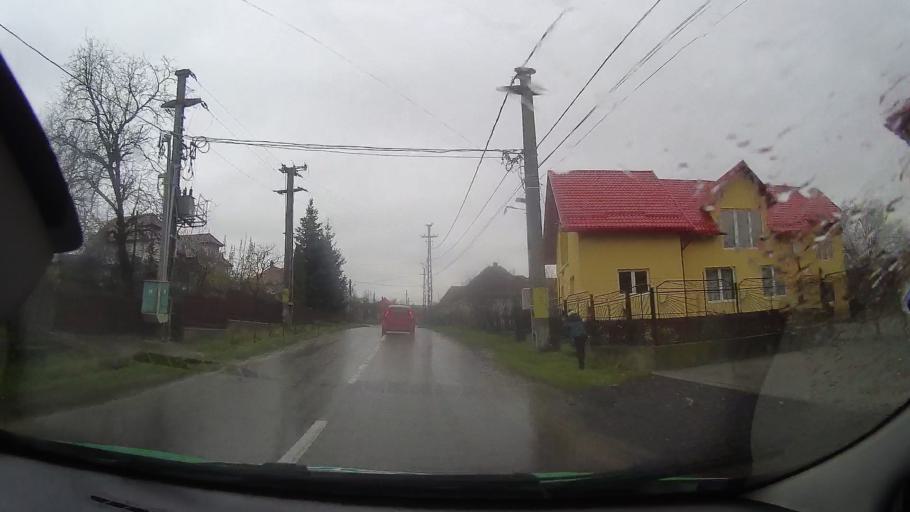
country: RO
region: Mures
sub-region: Comuna Vatava
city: Vatava
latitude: 46.9430
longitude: 24.7648
